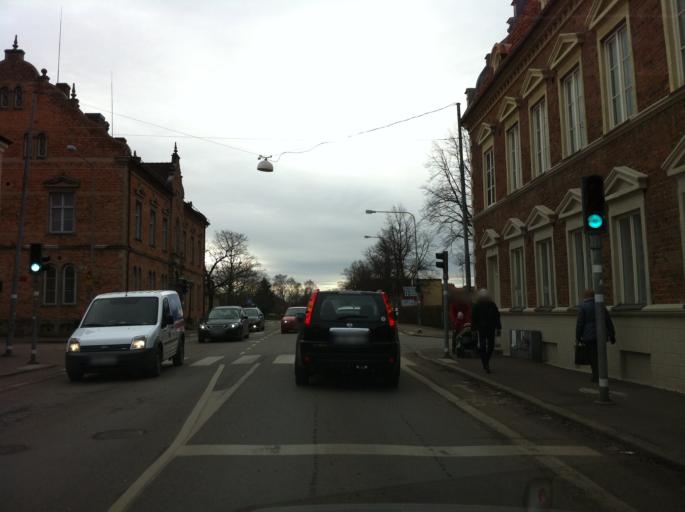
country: SE
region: Skane
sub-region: Angelholms Kommun
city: AEngelholm
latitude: 56.2461
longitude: 12.8662
